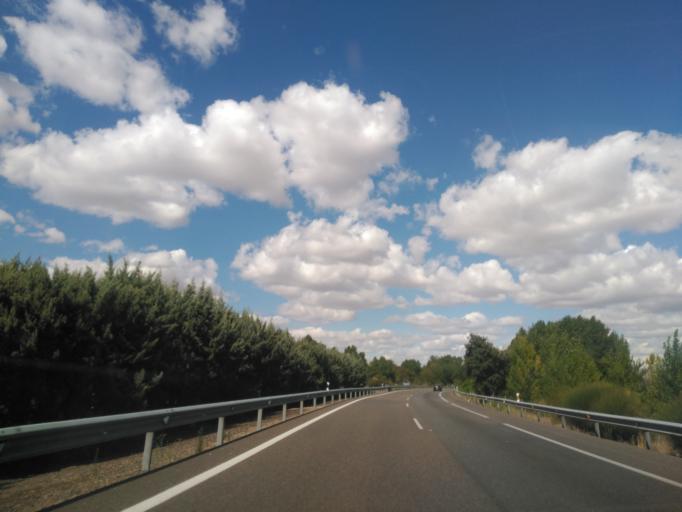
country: ES
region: Castille and Leon
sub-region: Provincia de Palencia
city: Duenas
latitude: 41.8779
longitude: -4.5405
